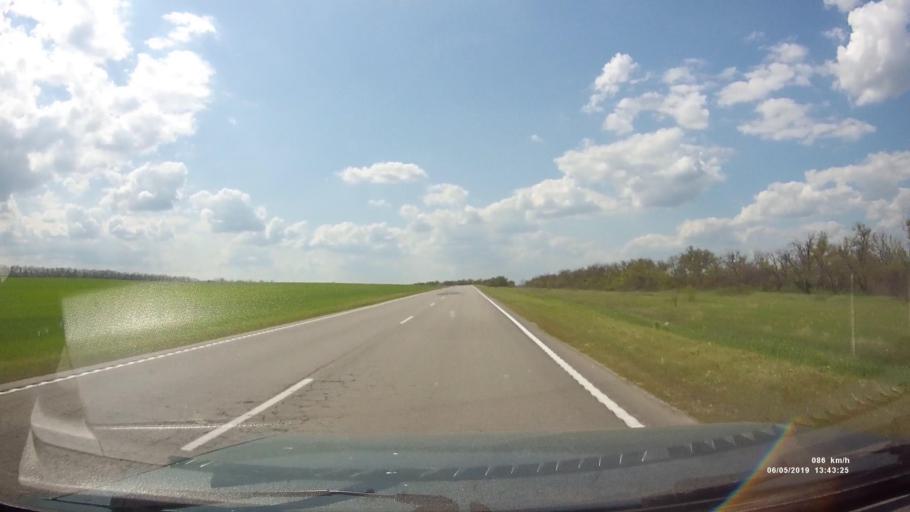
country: RU
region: Rostov
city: Semikarakorsk
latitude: 47.6605
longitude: 40.6387
